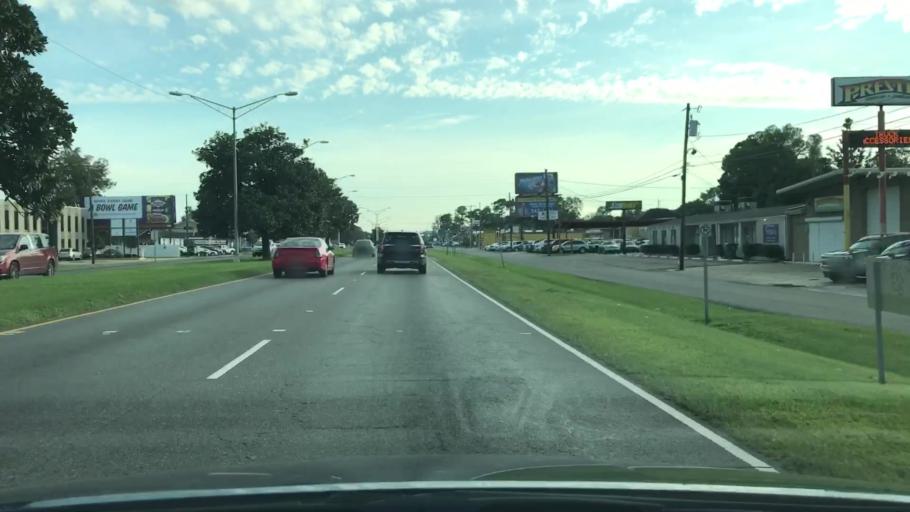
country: US
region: Louisiana
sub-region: Jefferson Parish
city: Metairie
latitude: 29.9869
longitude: -90.1560
